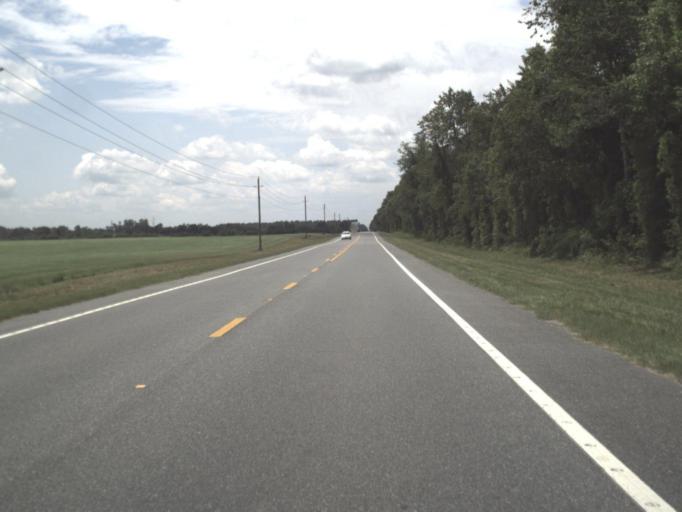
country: US
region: Florida
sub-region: Suwannee County
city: Wellborn
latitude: 30.0717
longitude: -82.9442
